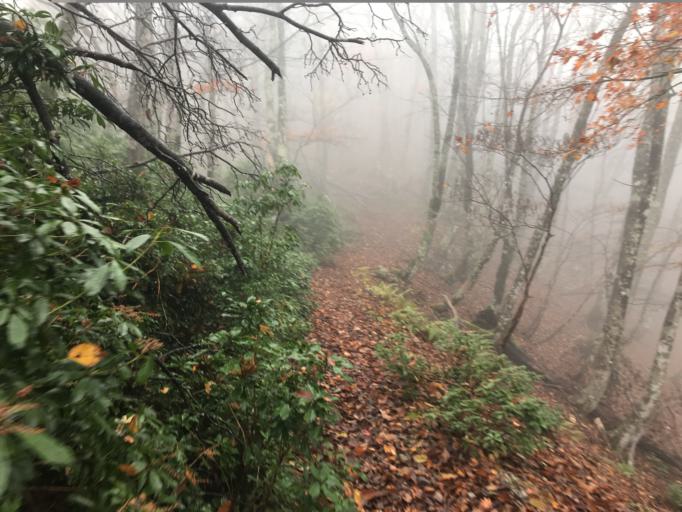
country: JP
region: Kyoto
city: Maizuru
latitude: 35.3088
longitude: 135.4585
